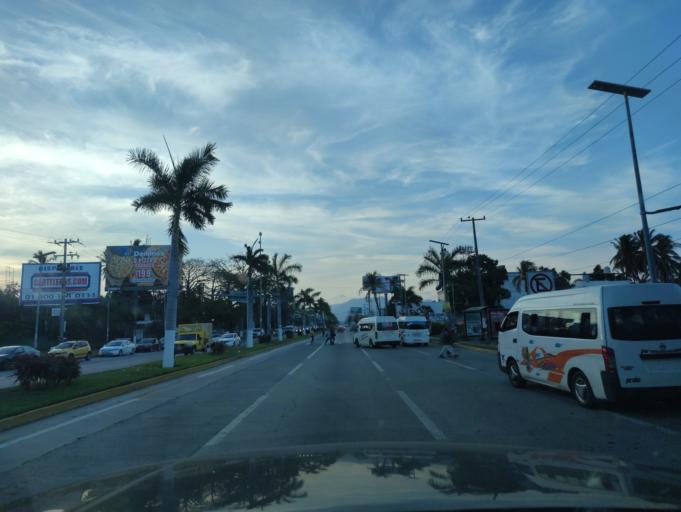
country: MX
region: Guerrero
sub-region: Acapulco de Juarez
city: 10 de Abril
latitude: 16.7745
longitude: -99.7767
